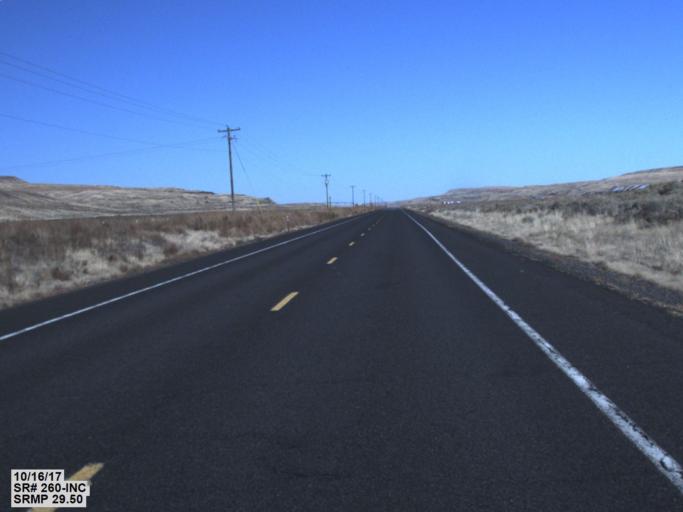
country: US
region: Washington
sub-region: Franklin County
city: Connell
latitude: 46.6700
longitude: -118.4714
